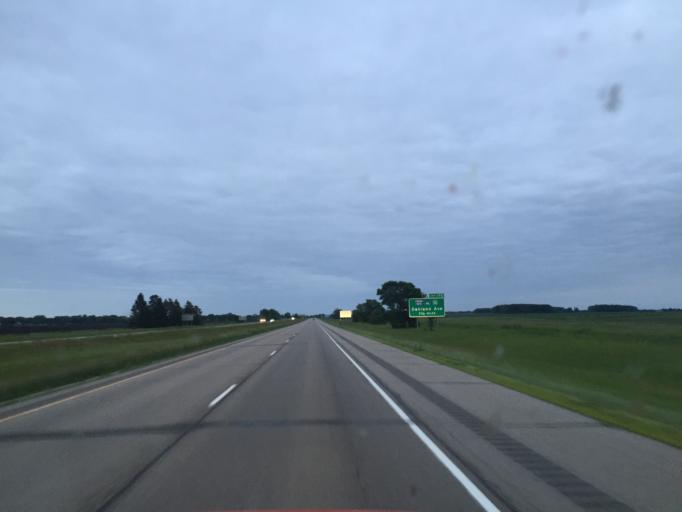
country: US
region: Minnesota
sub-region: Mower County
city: Austin
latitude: 43.6596
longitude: -93.0453
